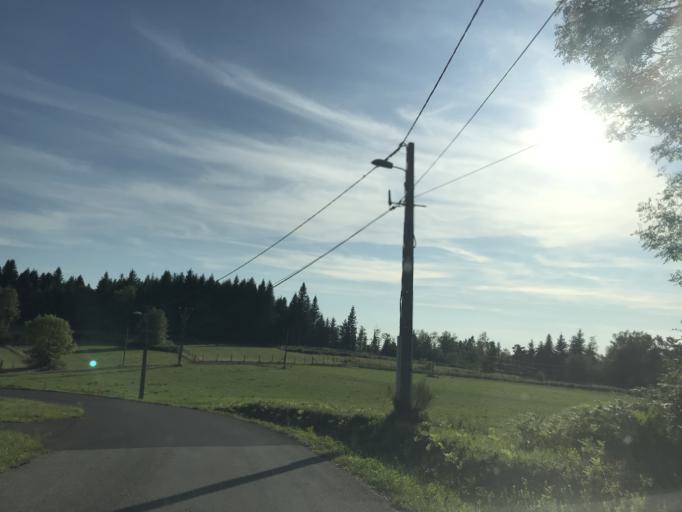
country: FR
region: Auvergne
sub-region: Departement du Puy-de-Dome
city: Job
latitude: 45.6764
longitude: 3.7411
